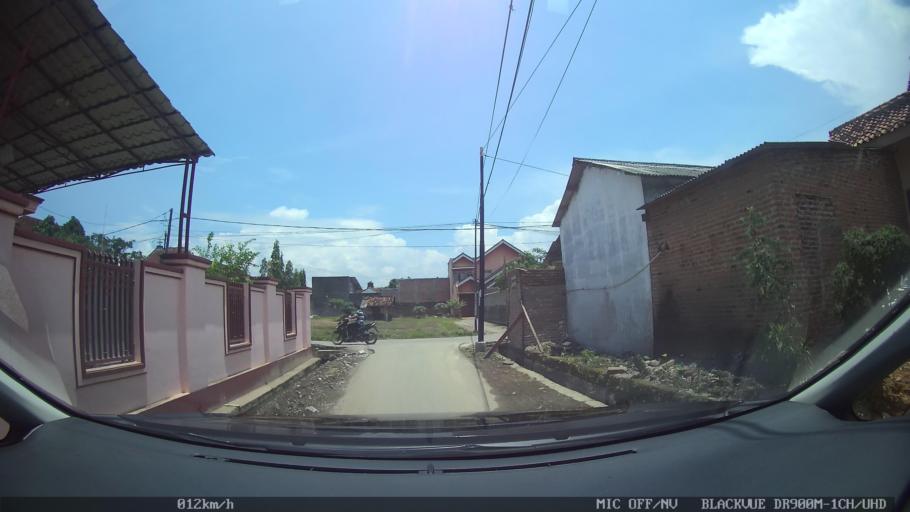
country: ID
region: Lampung
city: Kedaton
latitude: -5.3808
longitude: 105.2943
